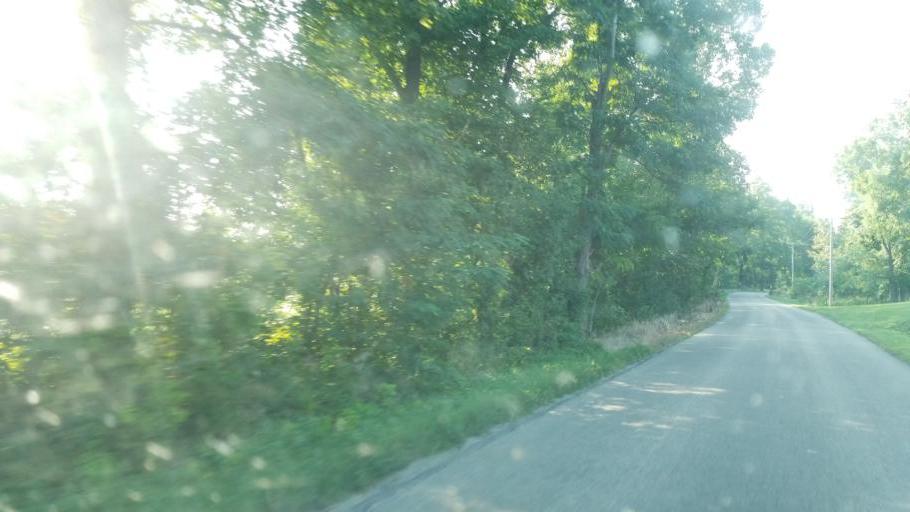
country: US
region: Ohio
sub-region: Morrow County
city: Mount Gilead
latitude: 40.5631
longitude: -82.6943
